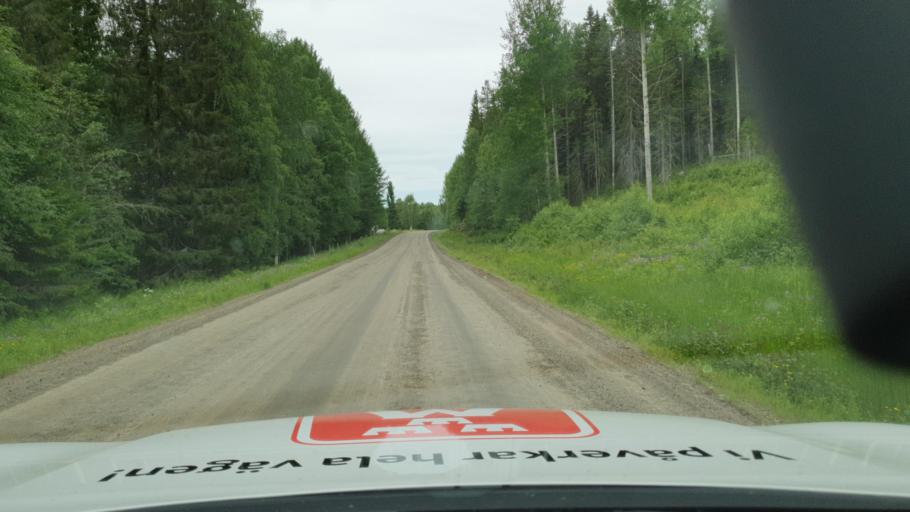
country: SE
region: Vaesterbotten
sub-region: Skelleftea Kommun
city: Burtraesk
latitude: 64.3316
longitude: 20.6191
